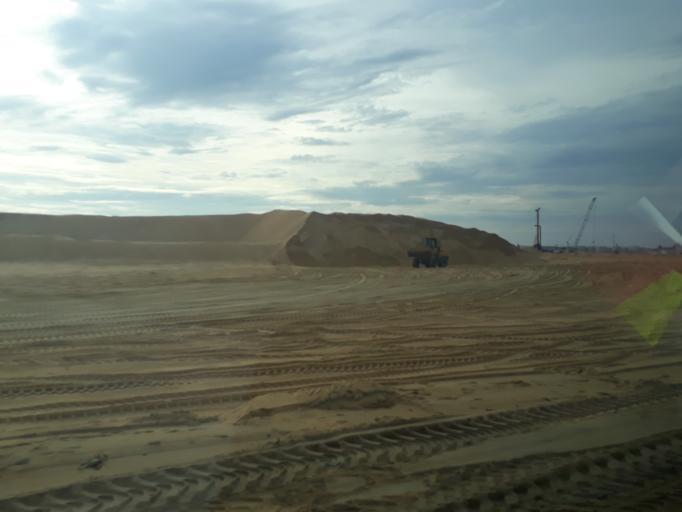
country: LK
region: Western
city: Colombo
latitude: 6.9293
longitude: 79.8398
